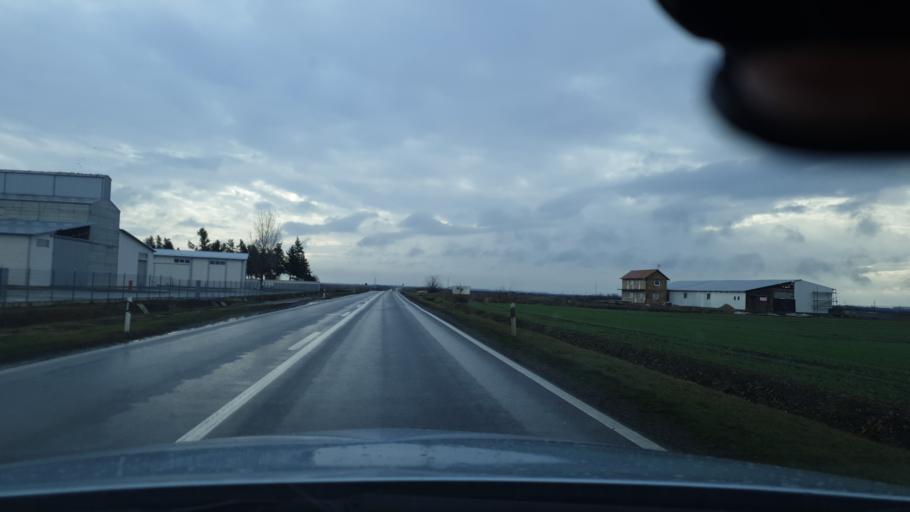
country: RS
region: Autonomna Pokrajina Vojvodina
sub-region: Juznobanatski Okrug
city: Kovin
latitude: 44.8061
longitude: 20.8949
